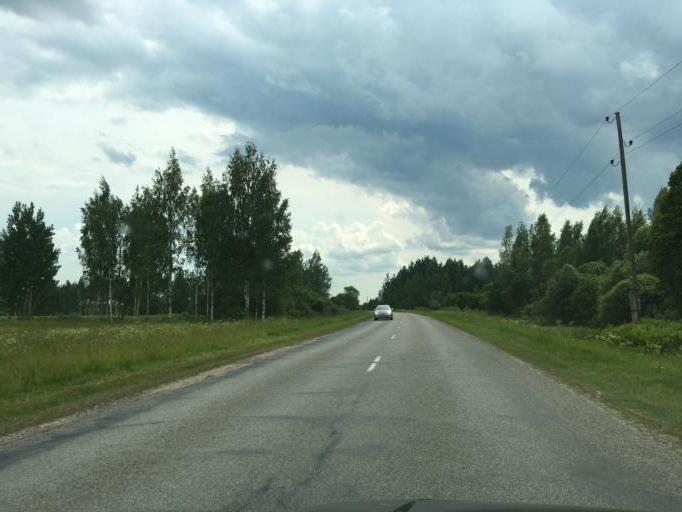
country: LV
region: Rugaju
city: Rugaji
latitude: 56.9382
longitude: 27.0665
